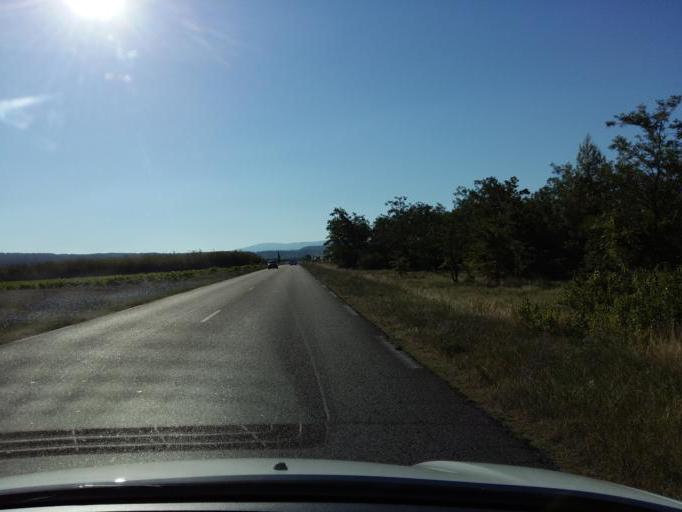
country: FR
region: Provence-Alpes-Cote d'Azur
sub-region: Departement du Vaucluse
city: Maubec
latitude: 43.8635
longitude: 5.1713
